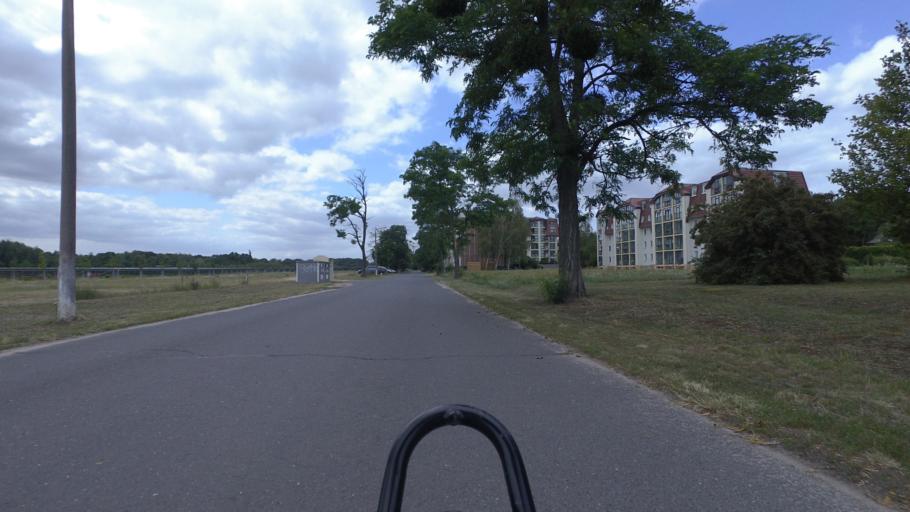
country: DE
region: Brandenburg
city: Trebbin
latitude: 52.2404
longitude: 13.1498
